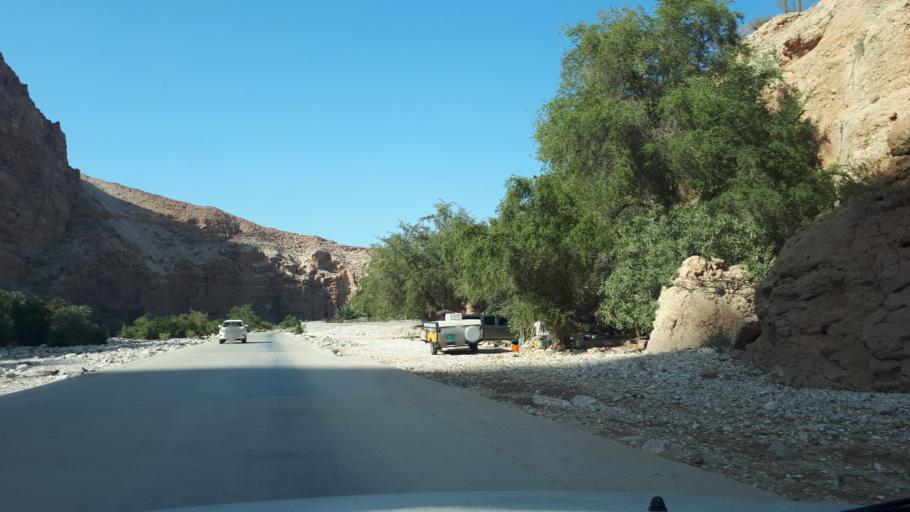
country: OM
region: Ash Sharqiyah
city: Sur
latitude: 22.8206
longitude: 59.2565
